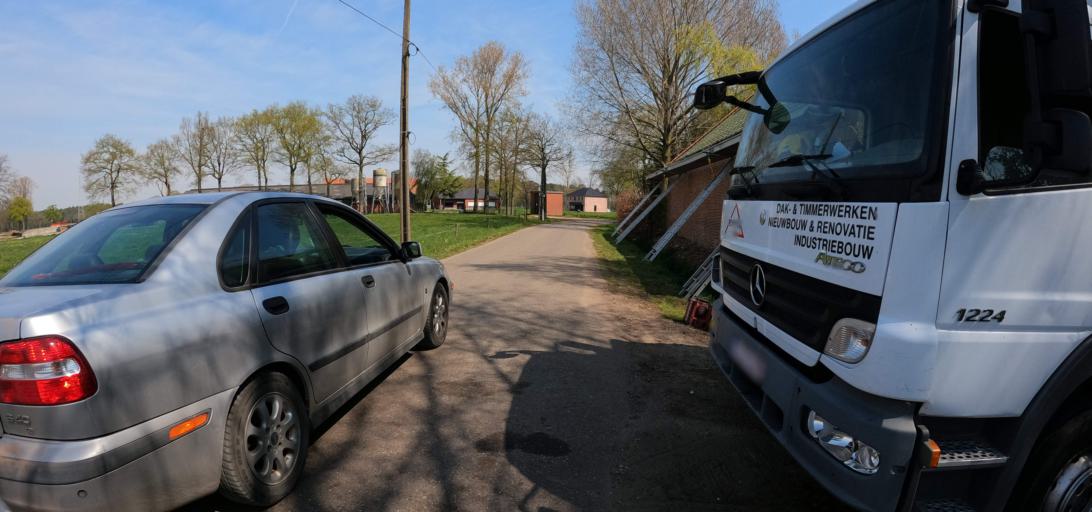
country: BE
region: Flanders
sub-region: Provincie Antwerpen
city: Vorselaar
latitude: 51.2289
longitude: 4.7741
